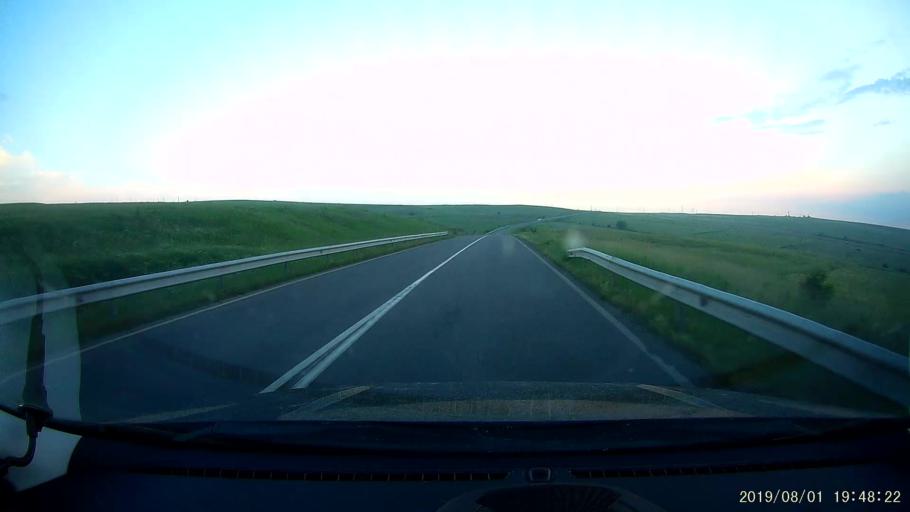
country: BG
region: Burgas
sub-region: Obshtina Karnobat
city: Karnobat
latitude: 42.6382
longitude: 26.9506
